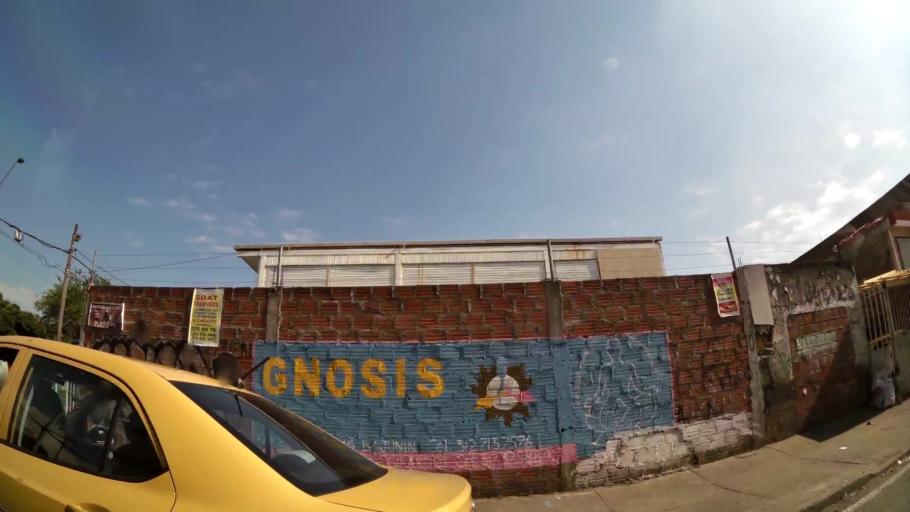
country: CO
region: Valle del Cauca
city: Cali
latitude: 3.4252
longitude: -76.5167
